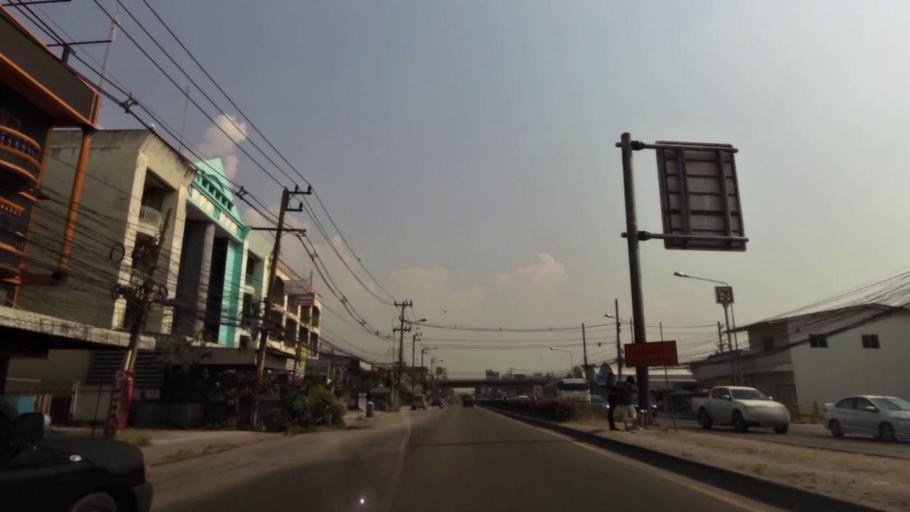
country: TH
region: Chon Buri
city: Chon Buri
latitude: 13.3526
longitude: 101.0060
